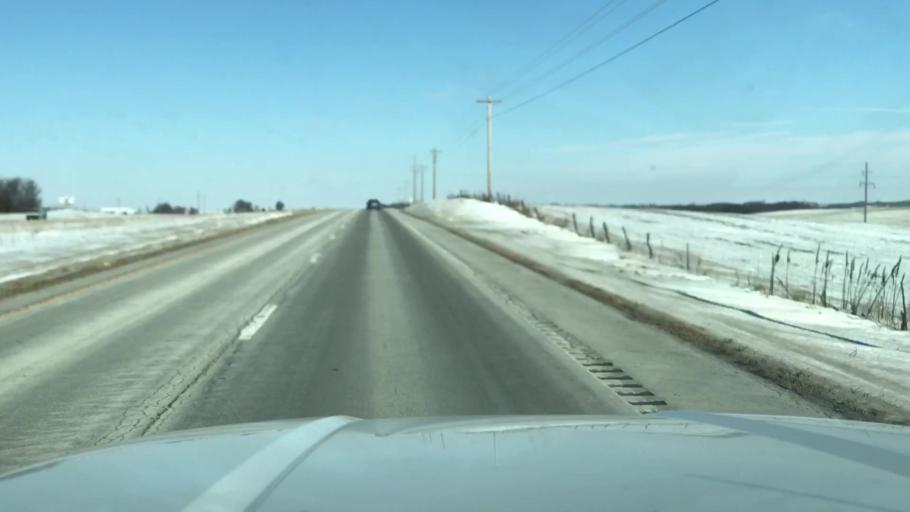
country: US
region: Missouri
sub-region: Andrew County
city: Savannah
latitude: 40.0034
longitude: -94.8797
